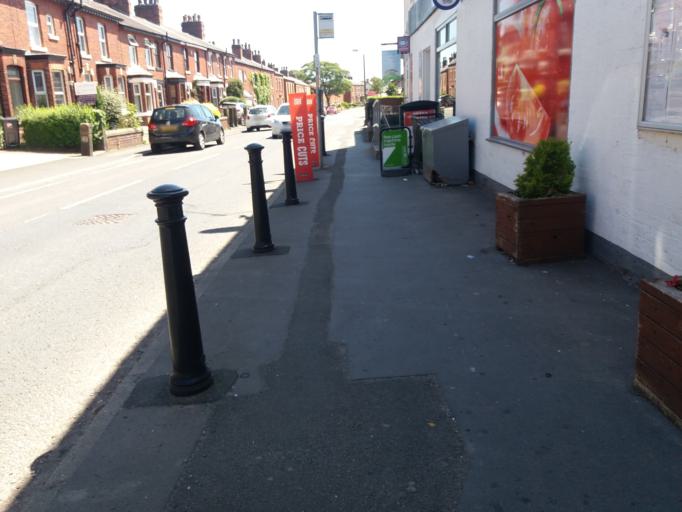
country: GB
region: England
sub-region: Lancashire
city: Croston
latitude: 53.6667
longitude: -2.7766
